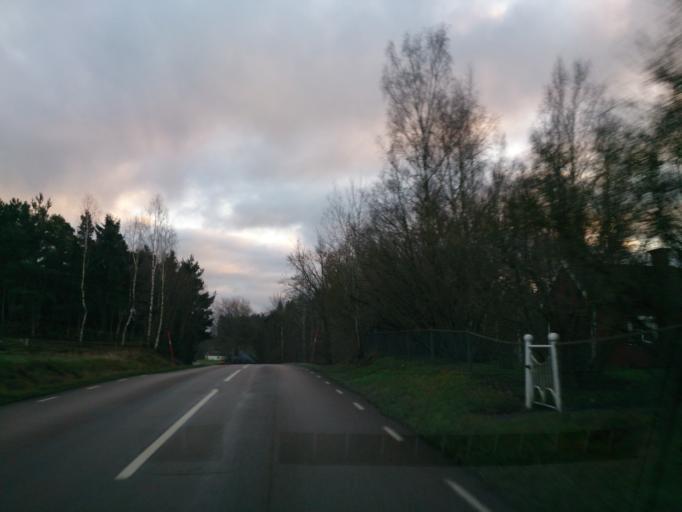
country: SE
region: OEstergoetland
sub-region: Norrkopings Kommun
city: Kimstad
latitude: 58.4202
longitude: 15.9141
